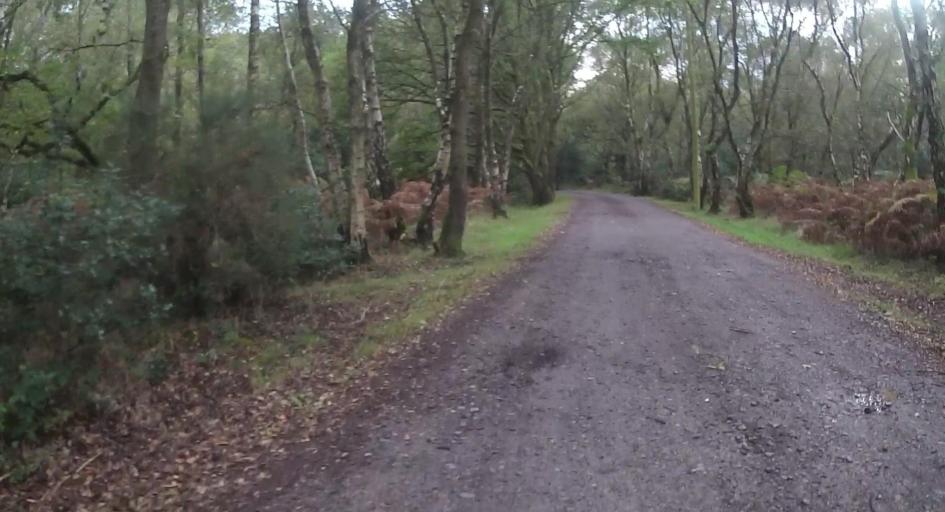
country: GB
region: England
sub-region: West Berkshire
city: Thatcham
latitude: 51.4187
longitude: -1.2288
